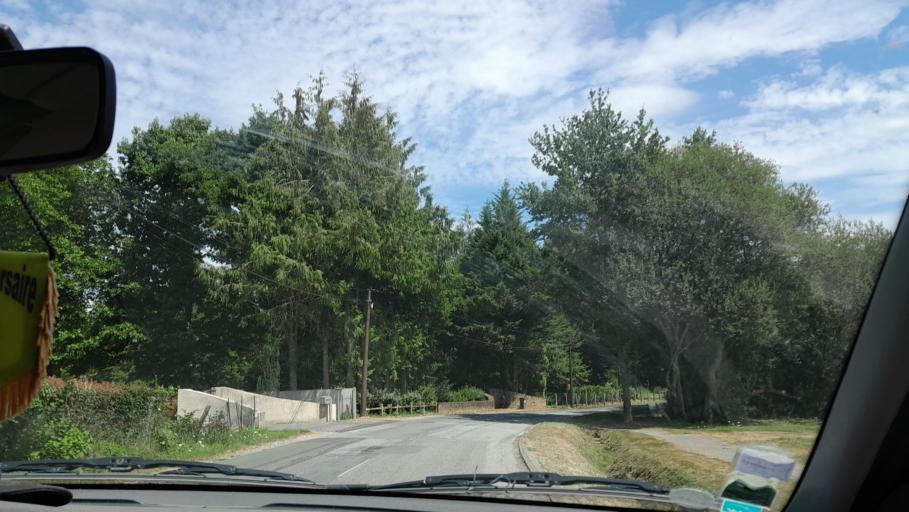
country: FR
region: Brittany
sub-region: Departement d'Ille-et-Vilaine
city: Le Pertre
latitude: 48.0702
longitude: -1.0200
